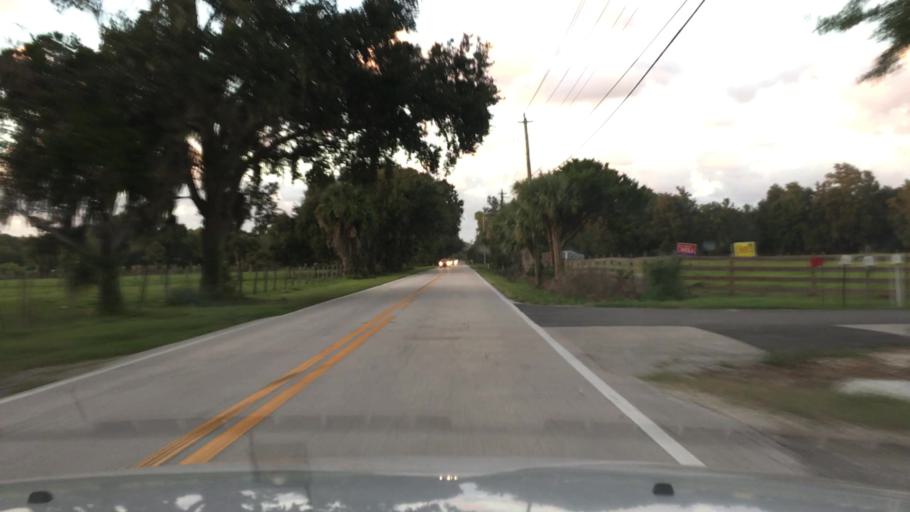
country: US
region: Florida
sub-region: Volusia County
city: Ormond Beach
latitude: 29.2815
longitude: -81.1130
